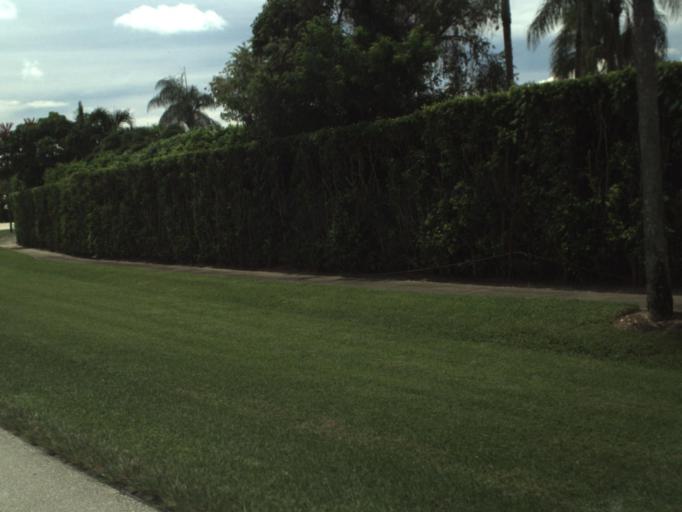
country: US
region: Florida
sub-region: Palm Beach County
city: Juno Beach
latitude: 26.8435
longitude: -80.0519
